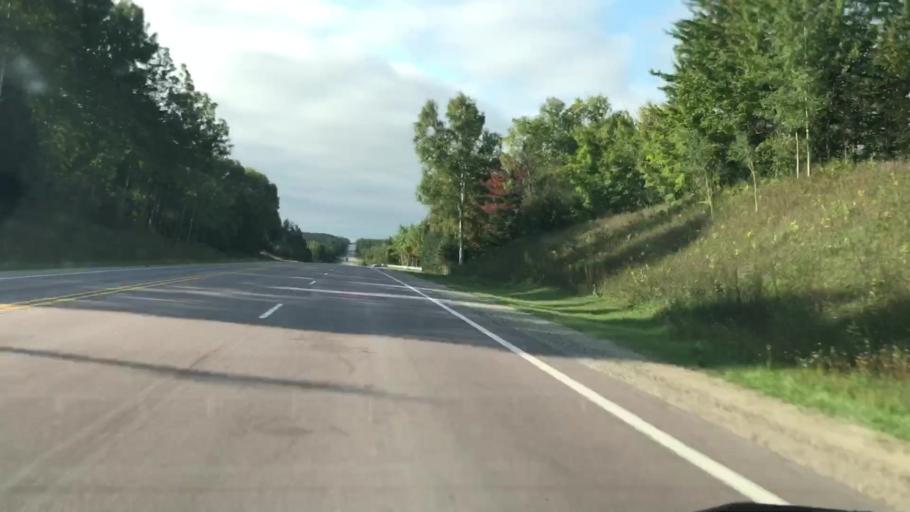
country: US
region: Michigan
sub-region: Luce County
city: Newberry
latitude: 46.3057
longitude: -85.5678
